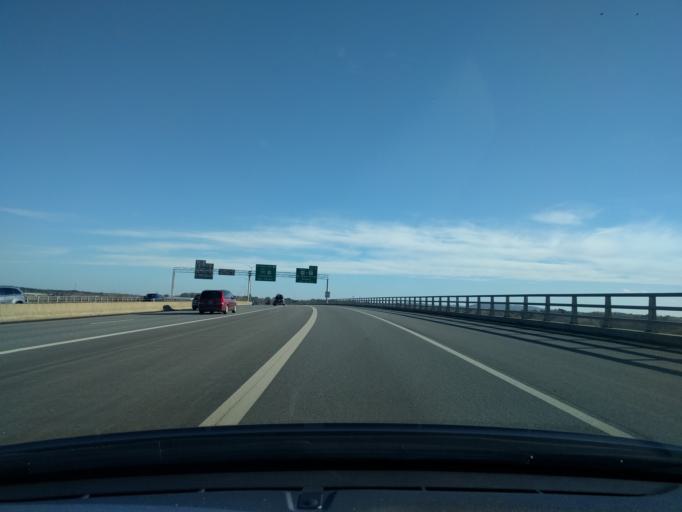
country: US
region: Maine
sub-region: Penobscot County
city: Bangor
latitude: 44.7847
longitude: -68.7777
